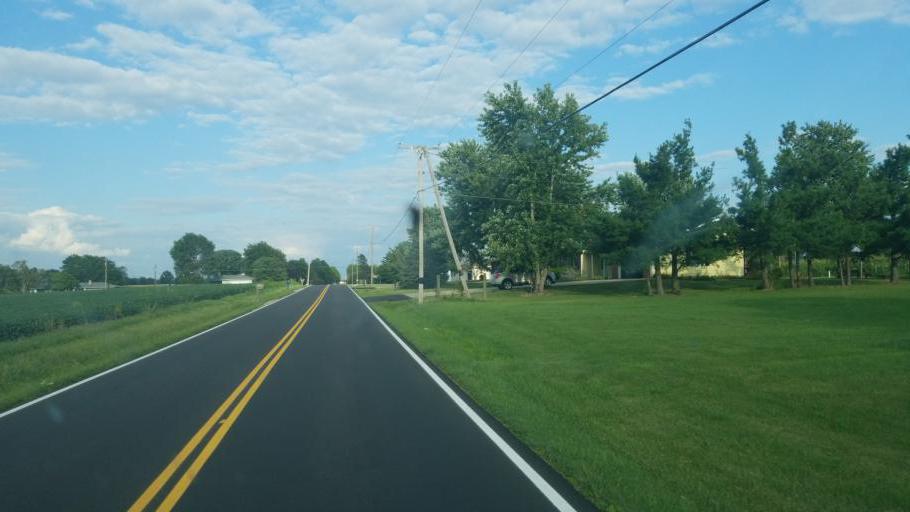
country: US
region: Ohio
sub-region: Seneca County
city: Tiffin
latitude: 41.1100
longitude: -83.0954
